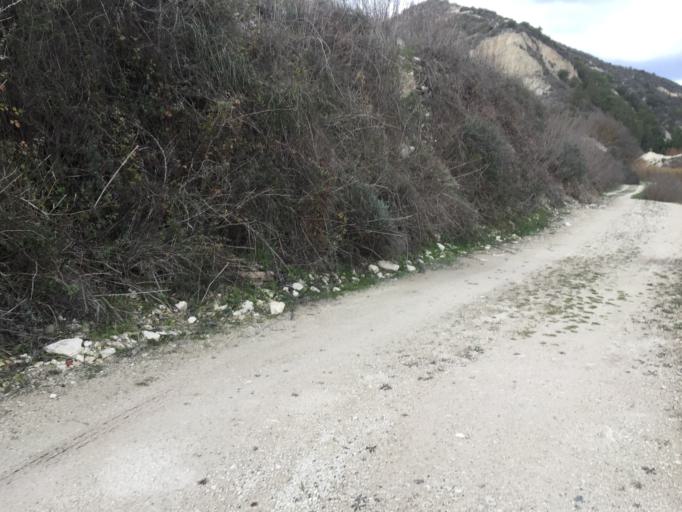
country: CY
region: Pafos
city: Mesogi
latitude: 34.8230
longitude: 32.5212
